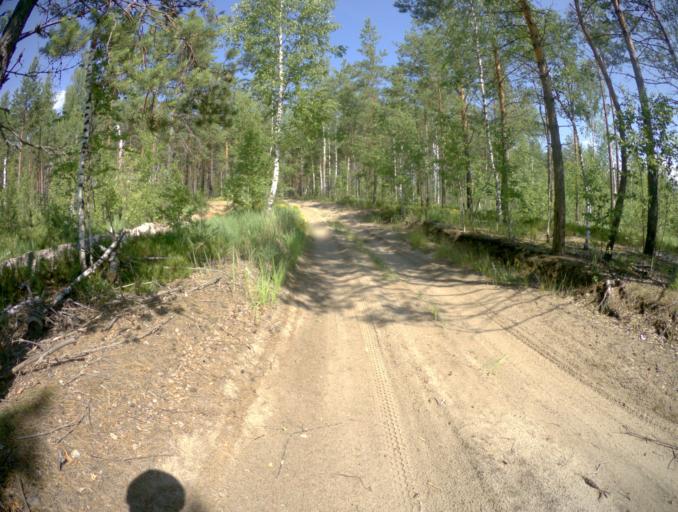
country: RU
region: Ivanovo
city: Talitsy
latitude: 56.4753
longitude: 42.2264
